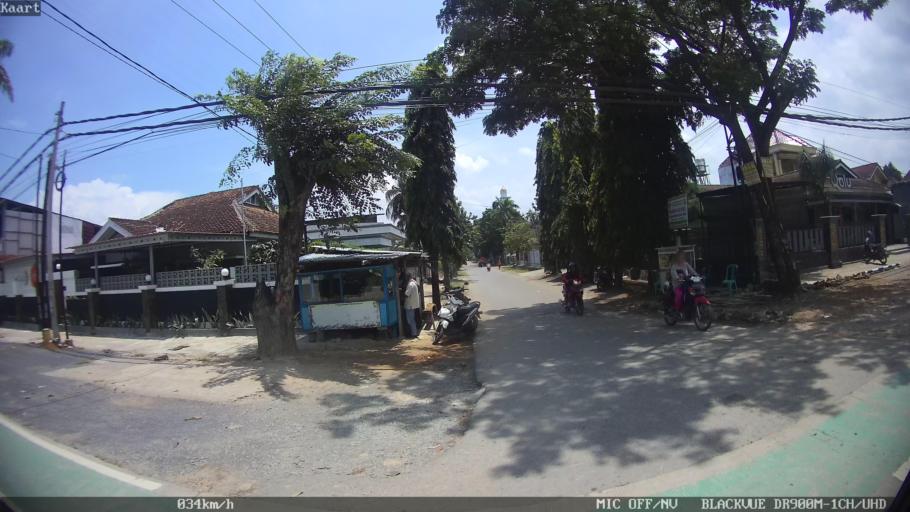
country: ID
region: Lampung
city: Kedaton
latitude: -5.3675
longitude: 105.2999
